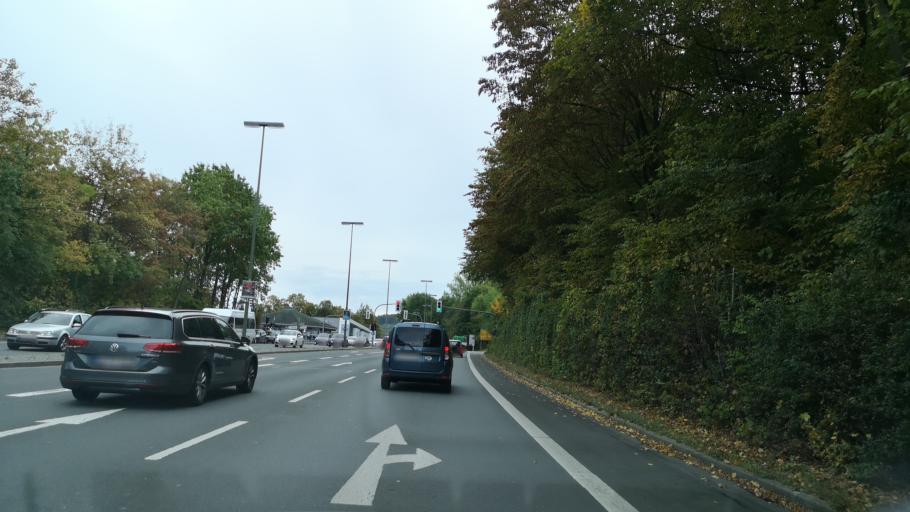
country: DE
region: North Rhine-Westphalia
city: Iserlohn
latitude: 51.3835
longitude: 7.7138
